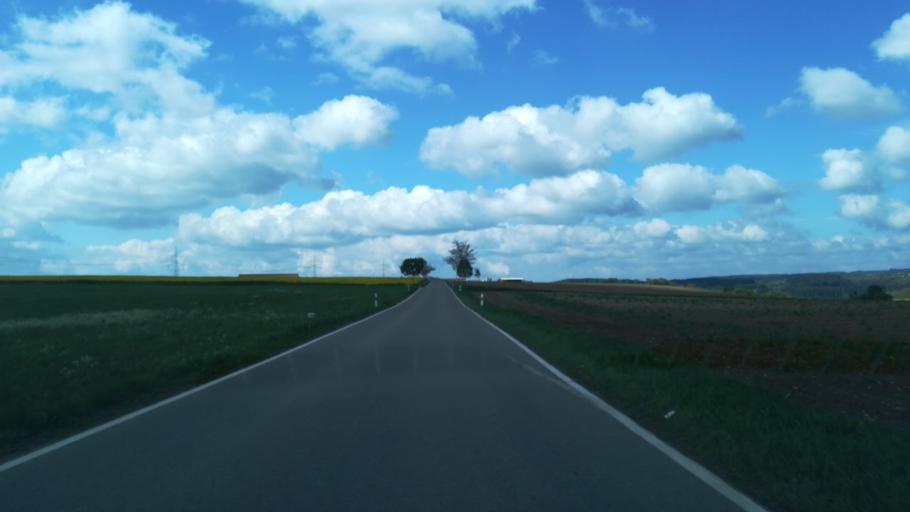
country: DE
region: Baden-Wuerttemberg
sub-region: Freiburg Region
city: Eggingen
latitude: 47.7600
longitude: 8.3778
